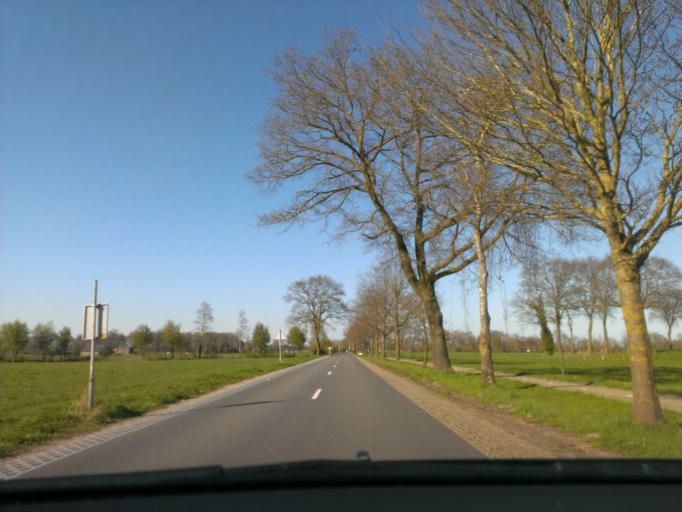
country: NL
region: Overijssel
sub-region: Gemeente Twenterand
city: Den Ham
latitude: 52.4397
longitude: 6.4744
